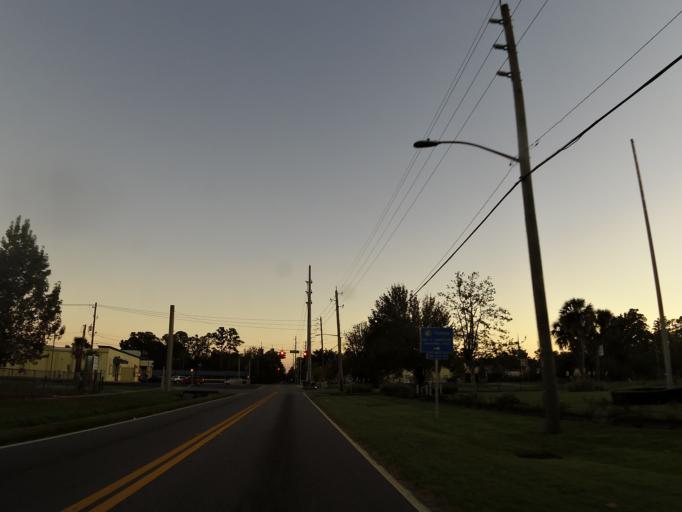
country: US
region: Florida
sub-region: Duval County
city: Jacksonville
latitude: 30.3102
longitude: -81.7436
